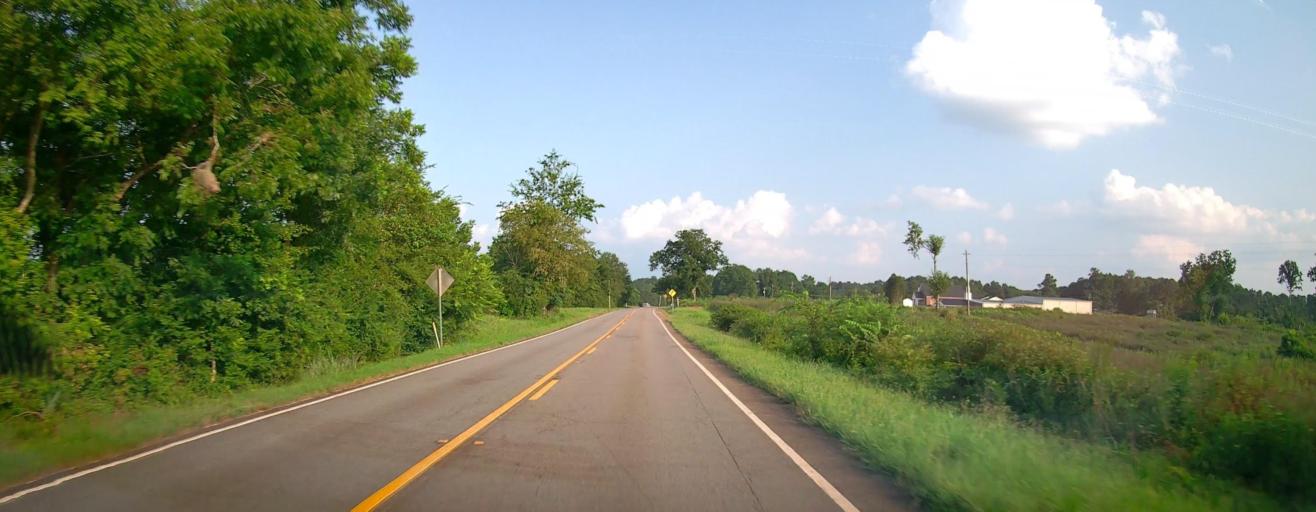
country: US
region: Georgia
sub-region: Jones County
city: Gray
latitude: 33.0571
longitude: -83.5611
